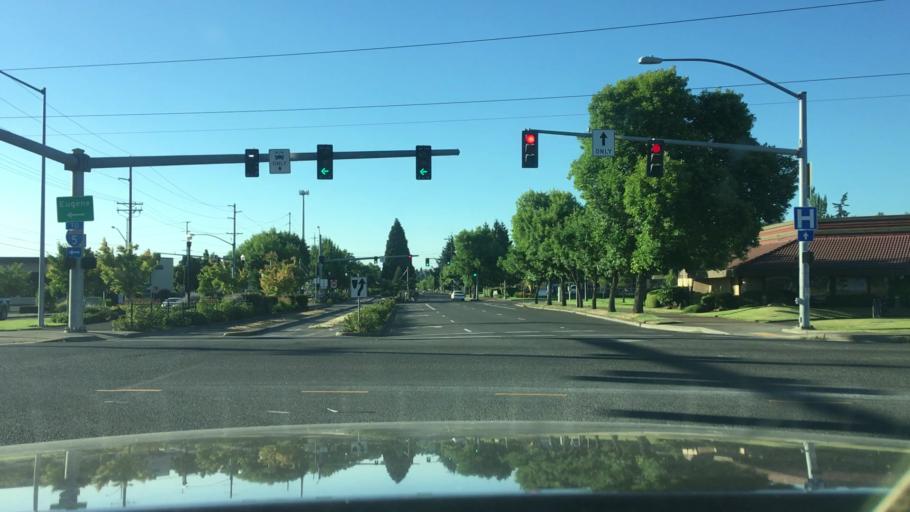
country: US
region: Oregon
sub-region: Lane County
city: Springfield
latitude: 44.0620
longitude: -123.0258
